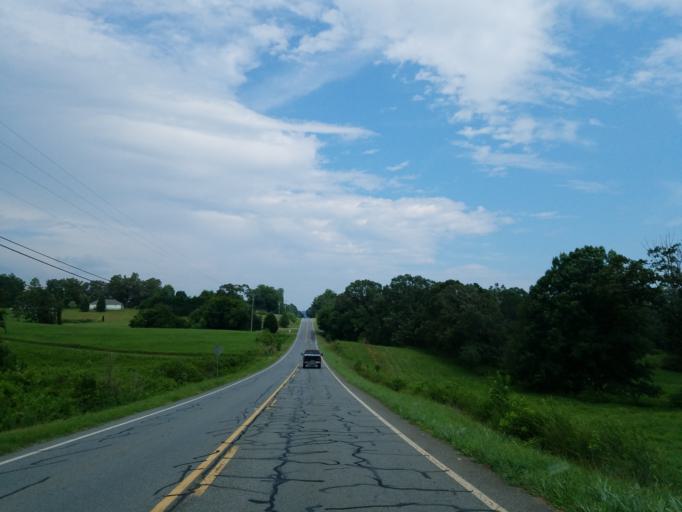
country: US
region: Georgia
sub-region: Gilmer County
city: Ellijay
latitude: 34.6435
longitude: -84.5499
